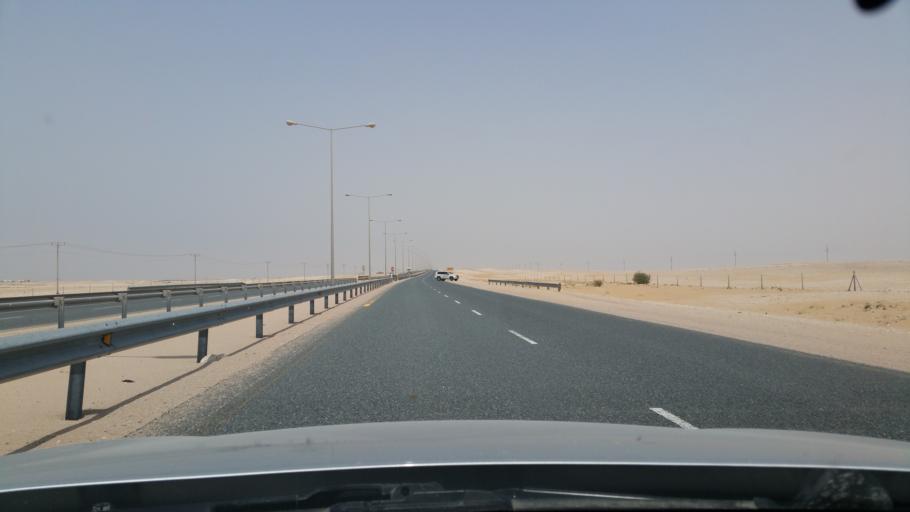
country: QA
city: Umm Bab
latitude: 25.0109
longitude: 50.9146
